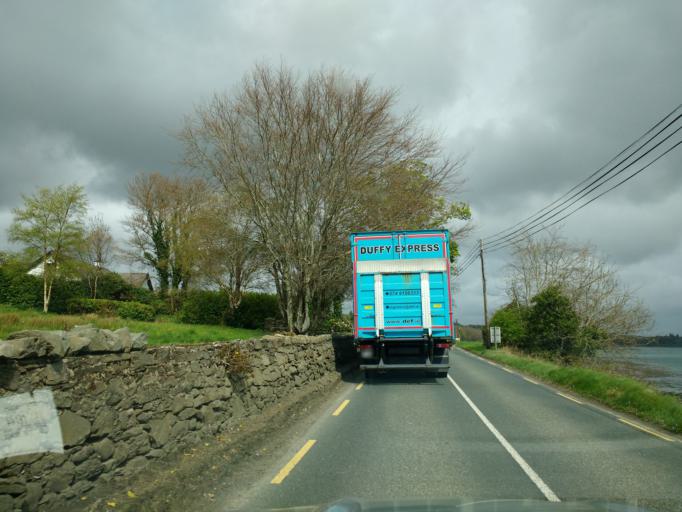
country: IE
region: Ulster
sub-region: County Donegal
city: Ramelton
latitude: 55.0783
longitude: -7.5905
